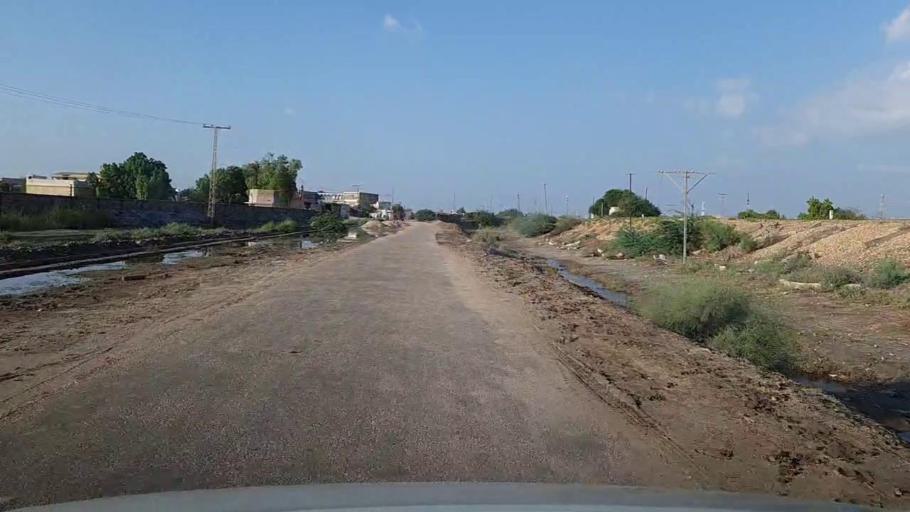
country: PK
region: Sindh
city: Hingorja
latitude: 27.0914
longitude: 68.4151
